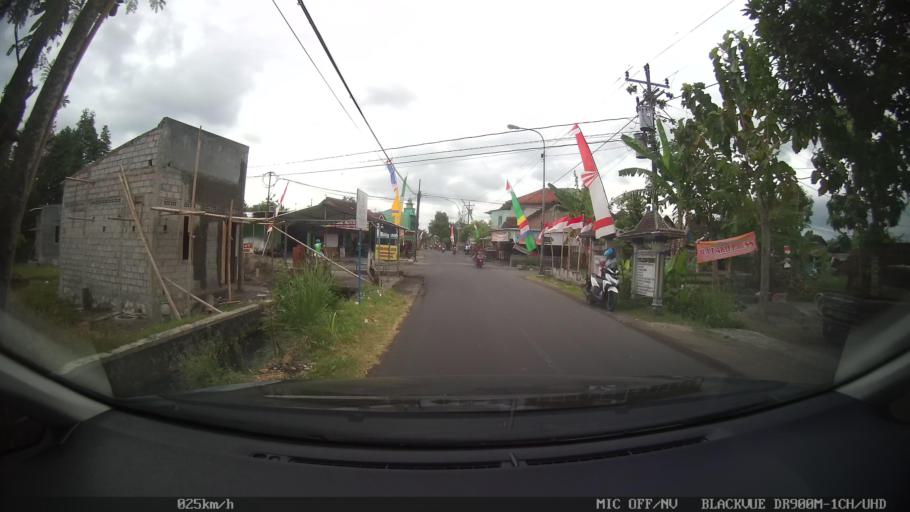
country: ID
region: Daerah Istimewa Yogyakarta
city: Sewon
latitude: -7.8354
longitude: 110.4189
